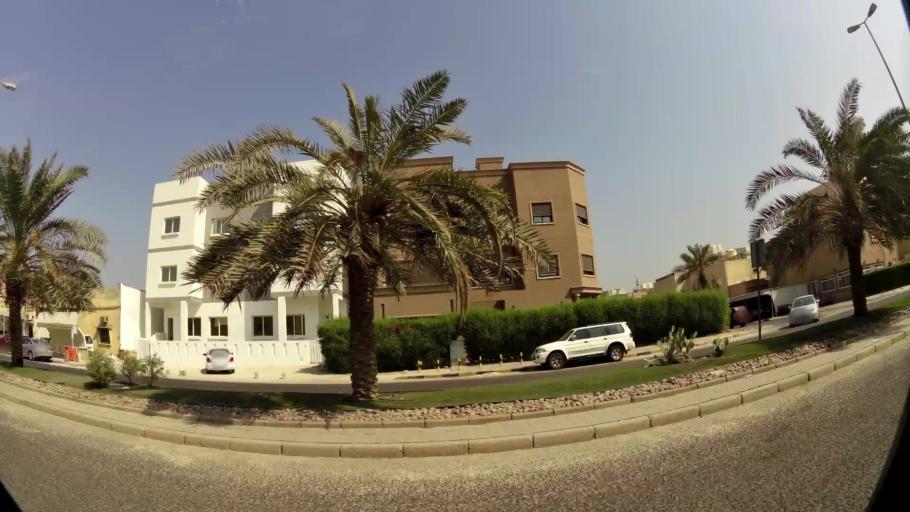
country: KW
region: Al Asimah
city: Ad Dasmah
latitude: 29.3476
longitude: 48.0069
